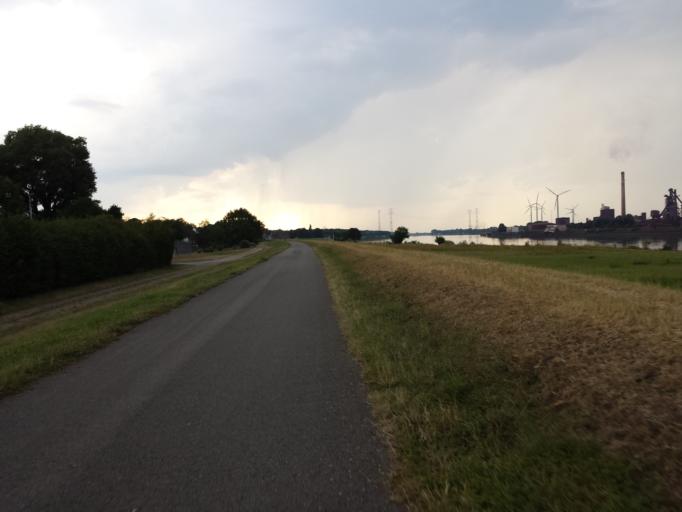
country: DE
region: Lower Saxony
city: Ritterhude
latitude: 53.1168
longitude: 8.7070
